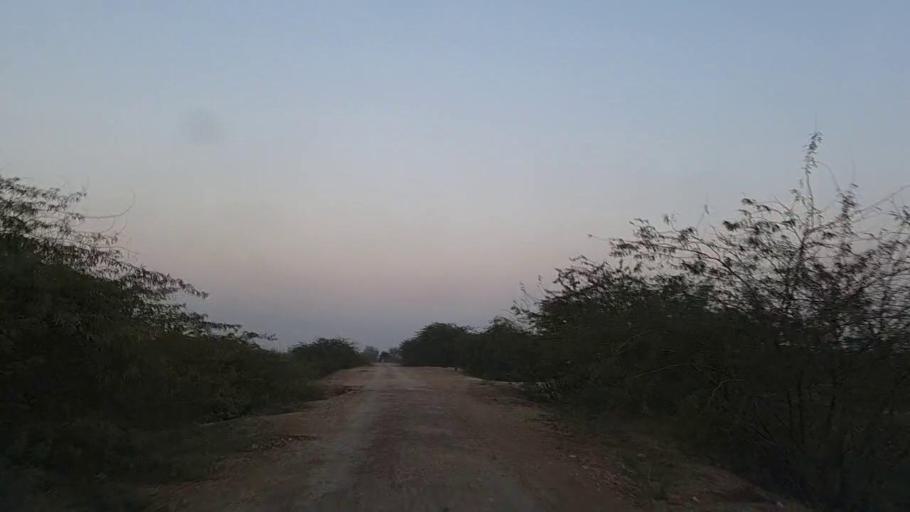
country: PK
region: Sindh
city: Bandhi
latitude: 26.6049
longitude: 68.3708
